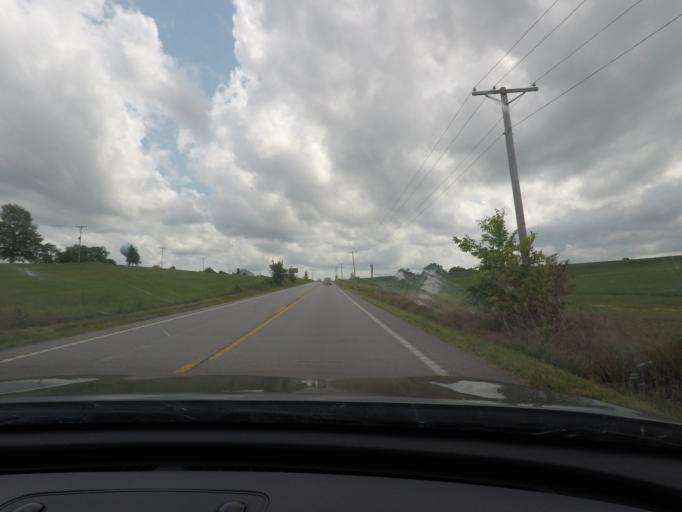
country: US
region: Missouri
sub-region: Lafayette County
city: Higginsville
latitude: 39.0072
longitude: -93.7351
